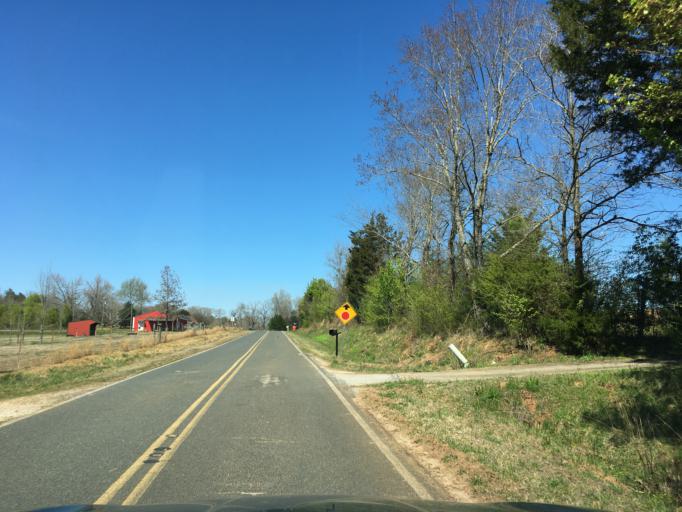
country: US
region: South Carolina
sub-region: Spartanburg County
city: Woodruff
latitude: 34.8276
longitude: -82.0793
